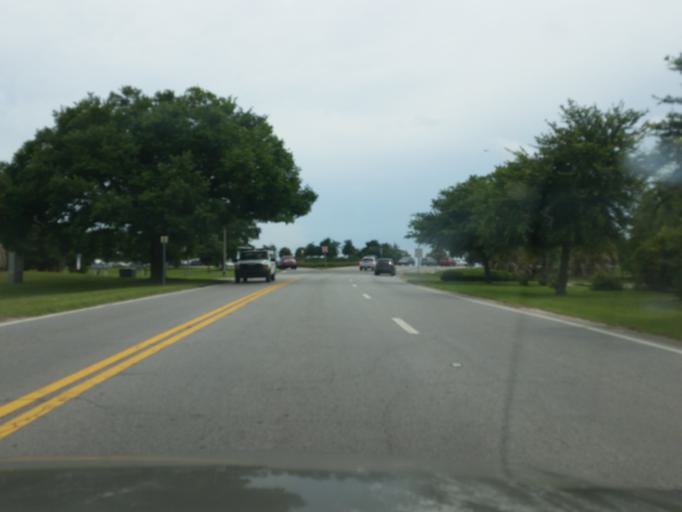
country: US
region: Florida
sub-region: Escambia County
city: East Pensacola Heights
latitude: 30.4193
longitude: -87.1941
